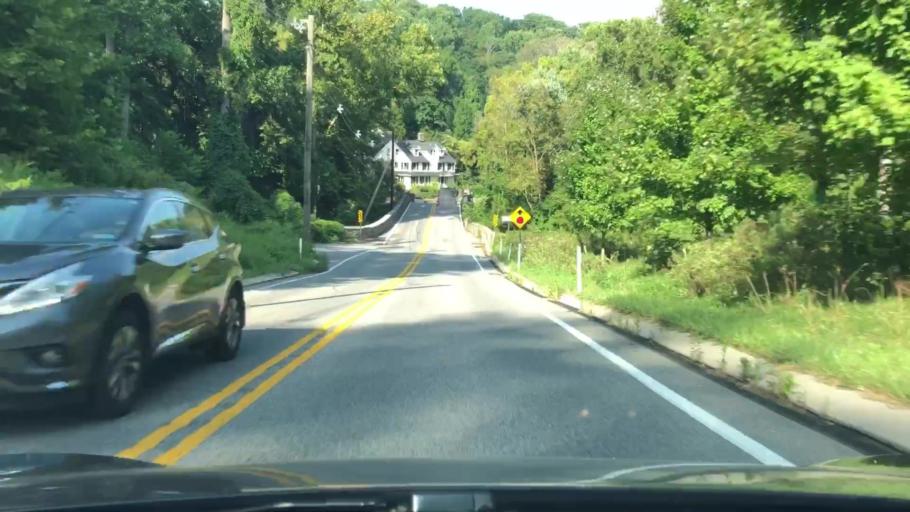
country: US
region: Pennsylvania
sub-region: Delaware County
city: Broomall
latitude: 40.0030
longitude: -75.3724
